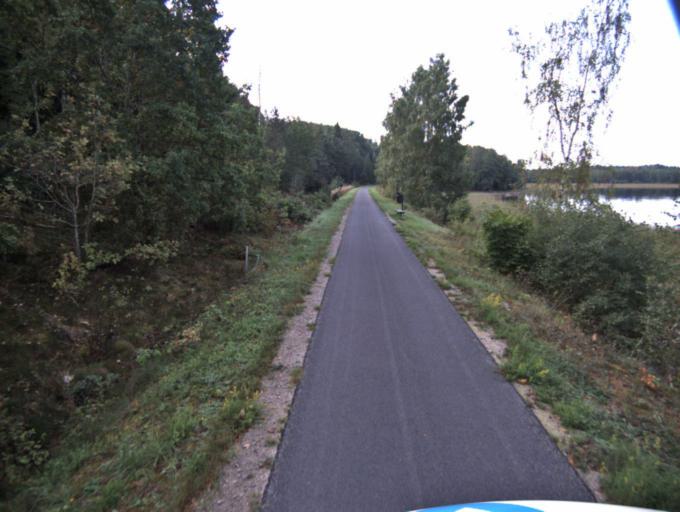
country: SE
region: Vaestra Goetaland
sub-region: Ulricehamns Kommun
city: Ulricehamn
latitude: 57.6980
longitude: 13.3932
